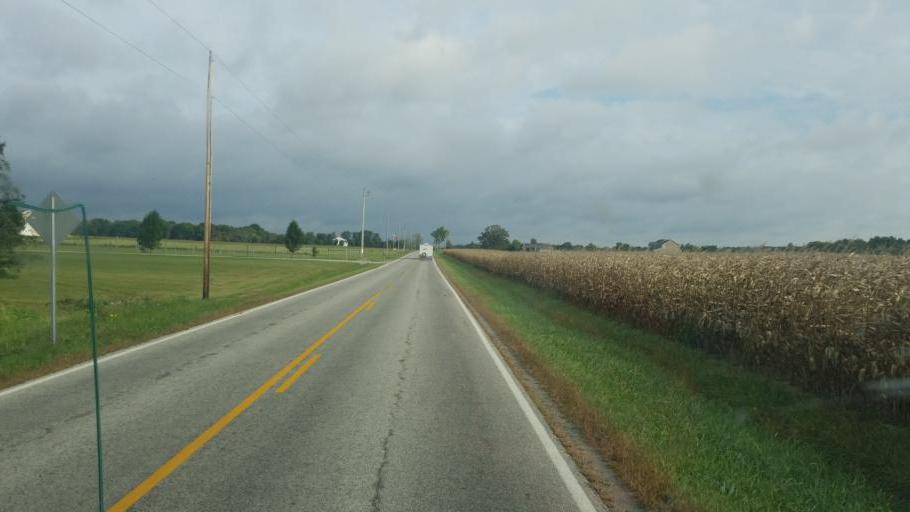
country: US
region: Ohio
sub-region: Wyandot County
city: Carey
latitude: 41.0368
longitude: -83.4774
